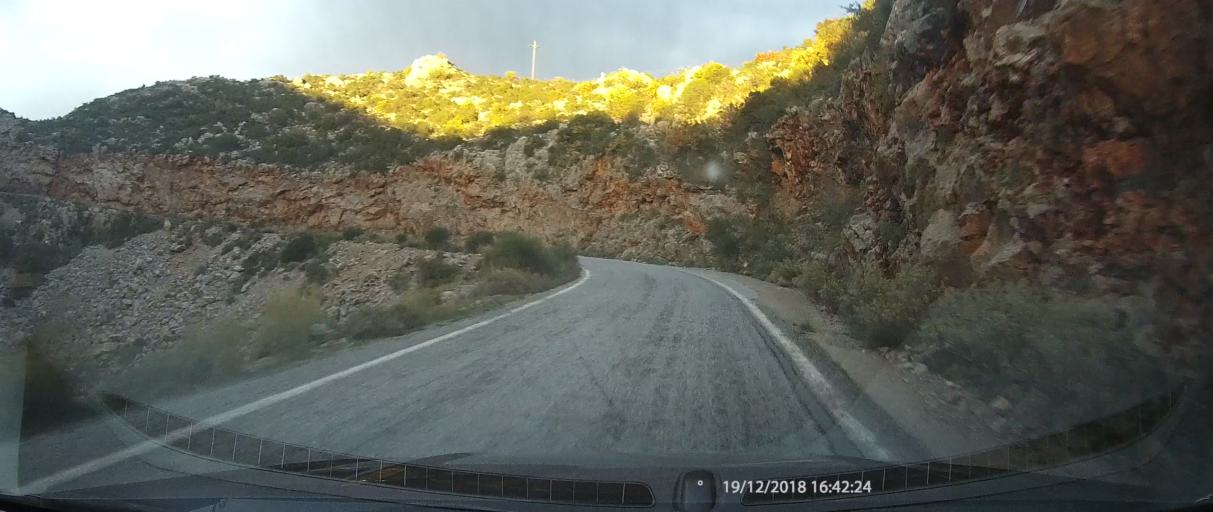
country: GR
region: Peloponnese
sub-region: Nomos Lakonias
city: Sykea
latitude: 36.9056
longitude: 22.9961
